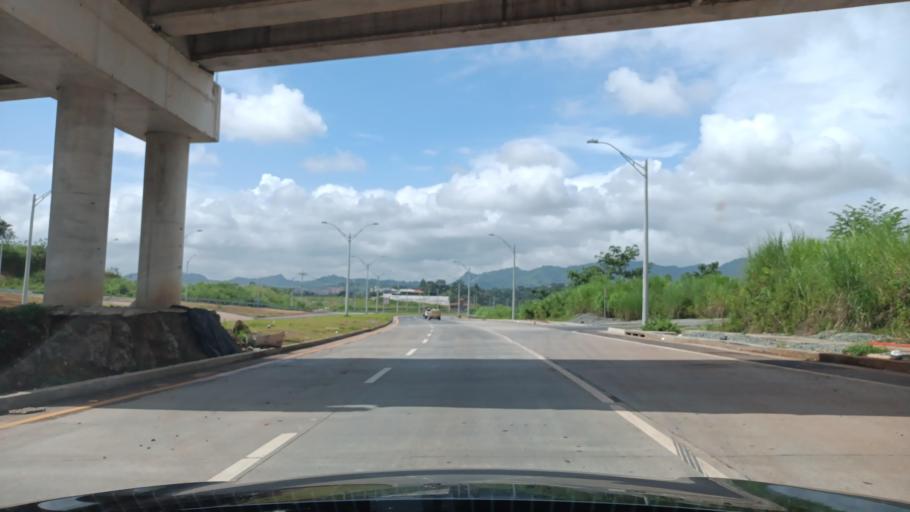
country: PA
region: Panama
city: Las Cumbres
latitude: 9.1017
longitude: -79.4983
